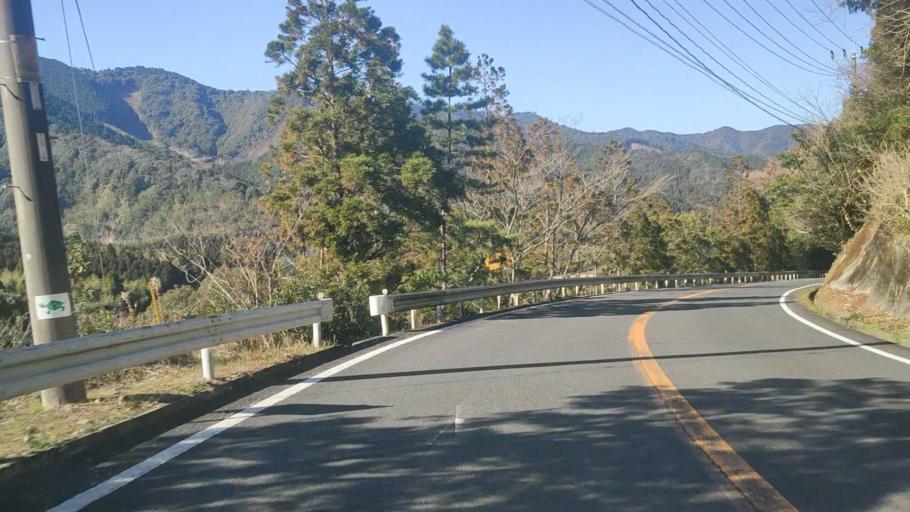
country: JP
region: Oita
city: Saiki
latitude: 32.8956
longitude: 131.9388
